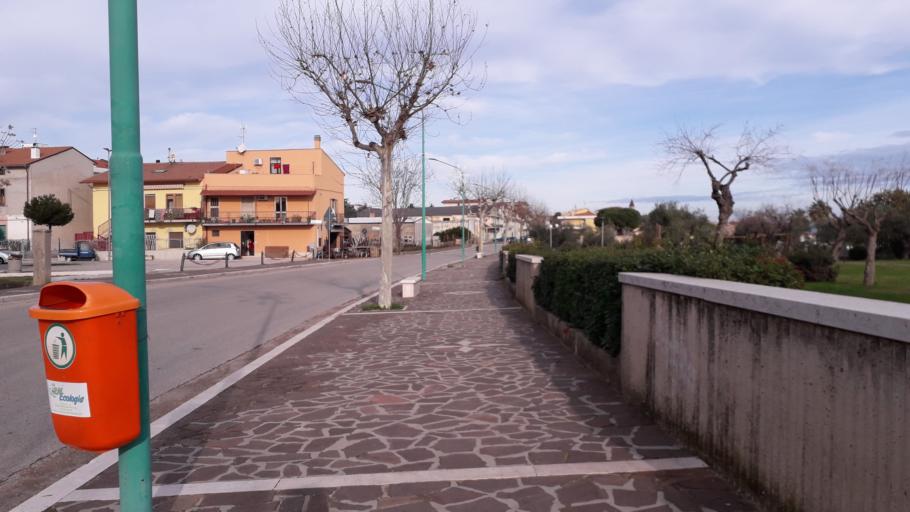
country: IT
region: Molise
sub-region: Provincia di Campobasso
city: Campomarino
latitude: 41.9532
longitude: 15.0358
